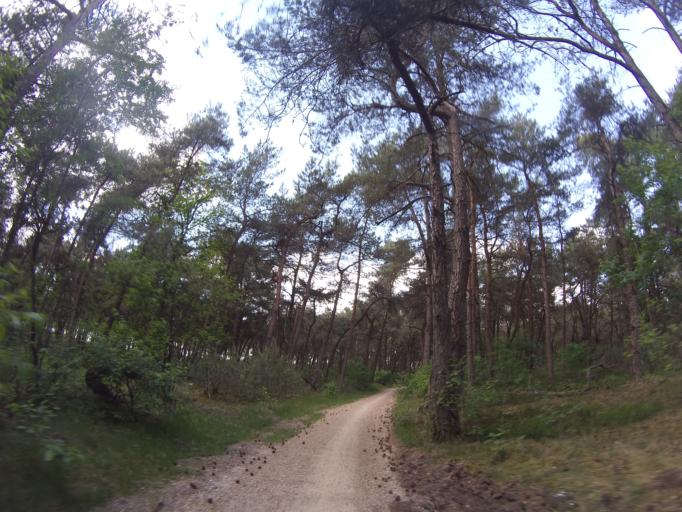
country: NL
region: Gelderland
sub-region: Gemeente Barneveld
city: Stroe
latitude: 52.1729
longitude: 5.7140
